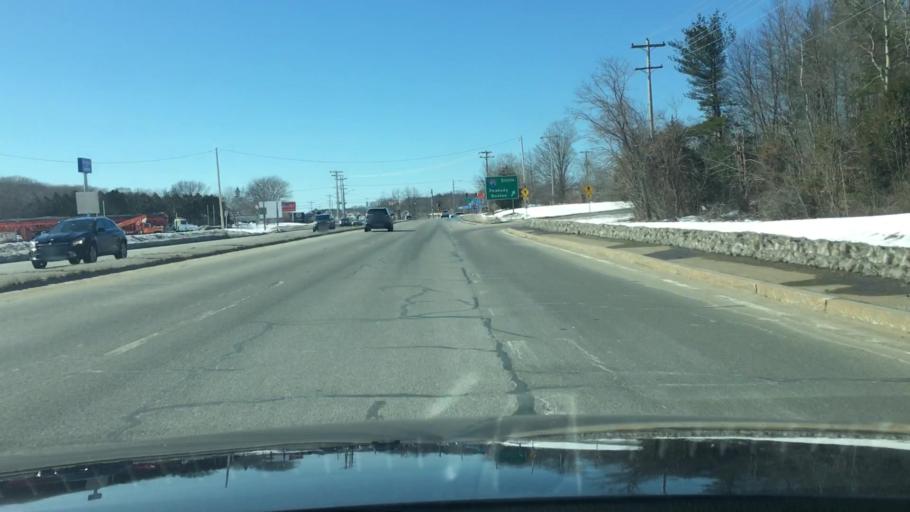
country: US
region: Massachusetts
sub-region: Essex County
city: Amesbury
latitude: 42.8454
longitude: -70.9037
